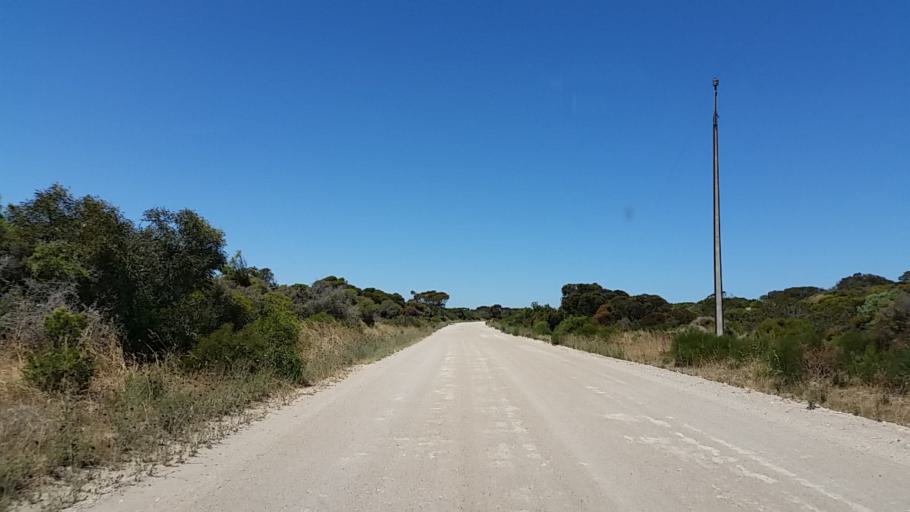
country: AU
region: South Australia
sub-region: Yorke Peninsula
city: Honiton
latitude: -35.1183
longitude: 137.3603
